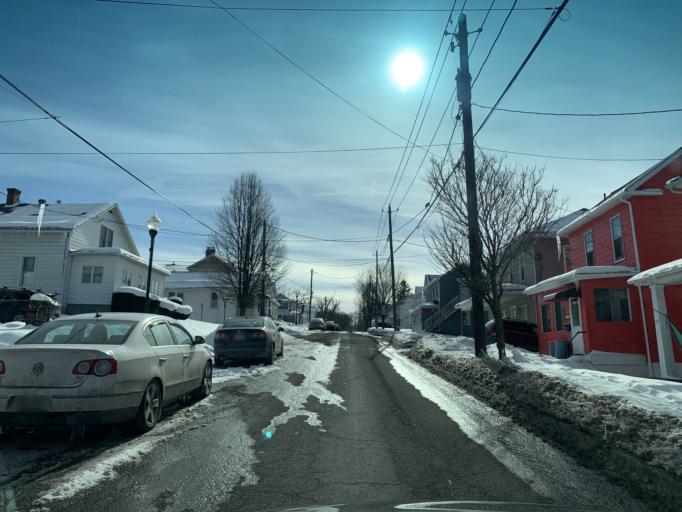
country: US
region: Maryland
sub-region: Allegany County
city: Frostburg
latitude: 39.6508
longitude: -78.9277
